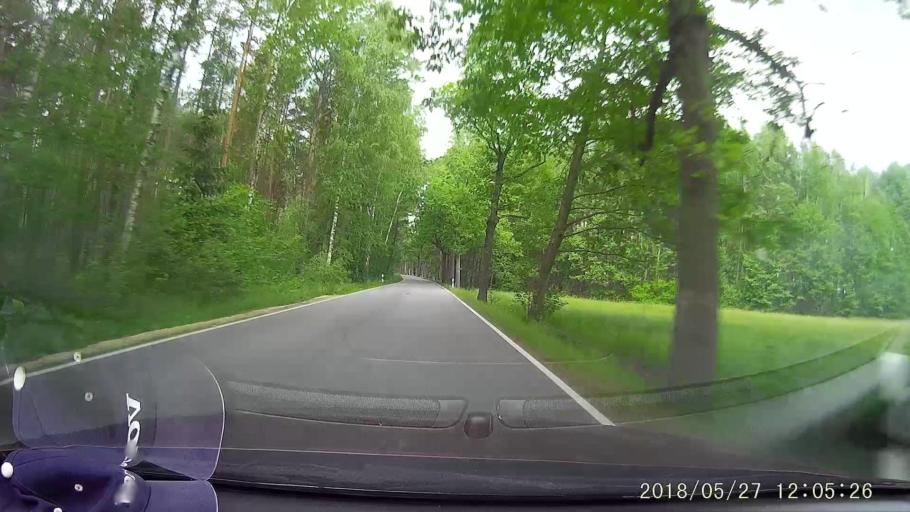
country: DE
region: Saxony
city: Mucka
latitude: 51.3450
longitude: 14.6631
